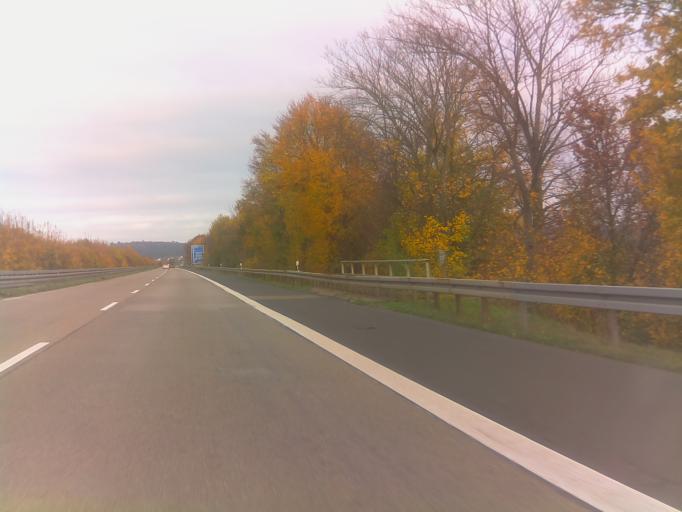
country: DE
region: Hesse
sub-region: Regierungsbezirk Darmstadt
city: Altenstadt
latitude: 50.2796
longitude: 8.9751
